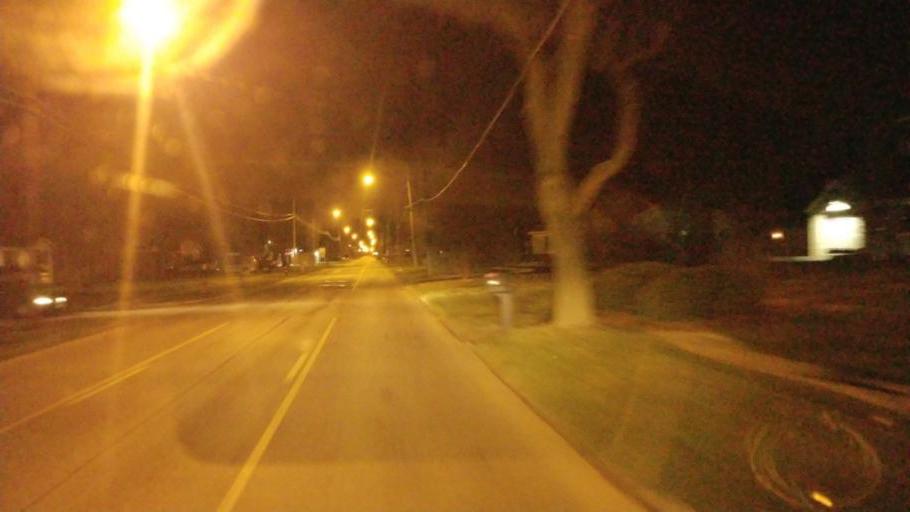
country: US
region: Ohio
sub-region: Crawford County
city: Bucyrus
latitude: 40.7945
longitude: -82.9770
